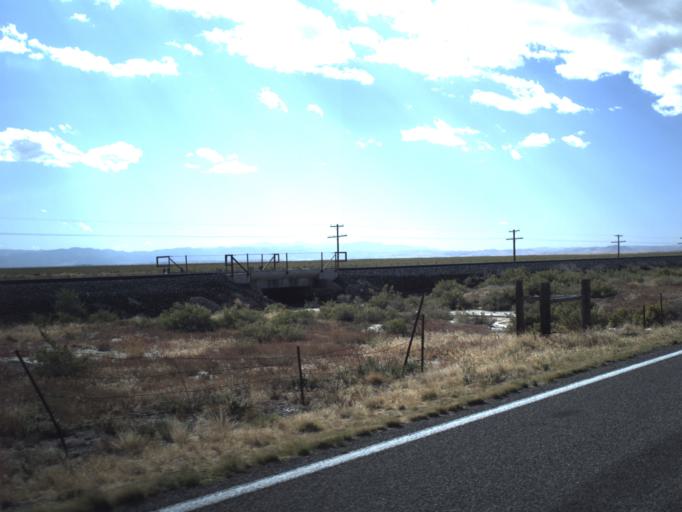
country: US
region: Utah
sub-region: Millard County
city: Delta
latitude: 39.0702
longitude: -112.7596
